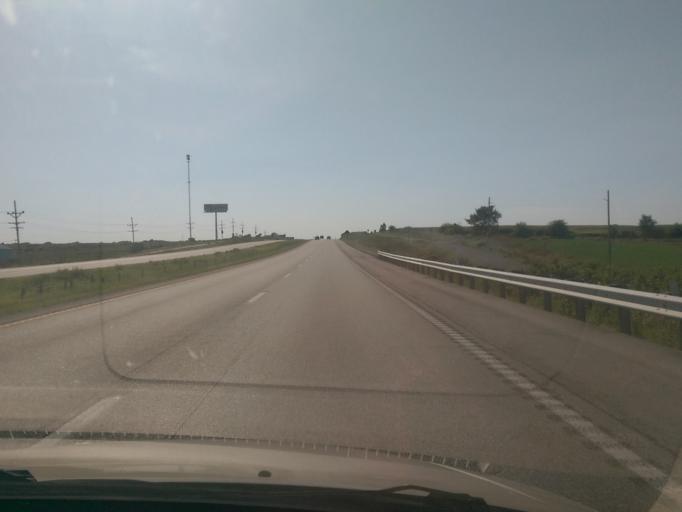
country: US
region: Missouri
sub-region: Saline County
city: Sweet Springs
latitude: 38.9806
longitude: -93.4740
